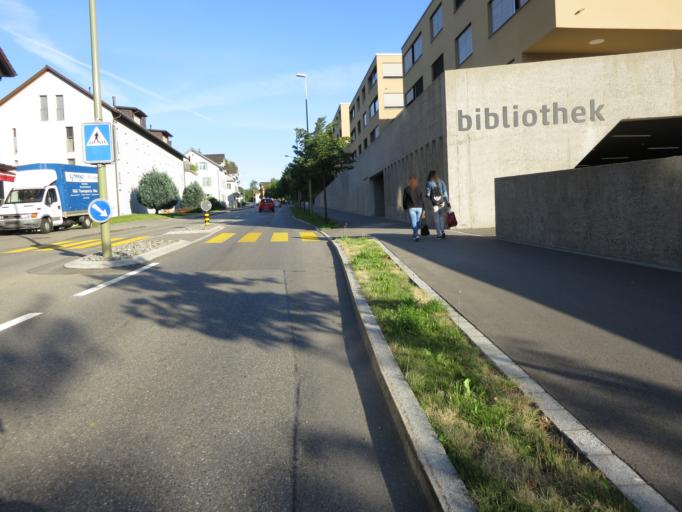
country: CH
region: Zurich
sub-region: Bezirk Hinwil
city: Rueti / Westlicher Dorfteil
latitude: 47.2593
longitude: 8.8477
